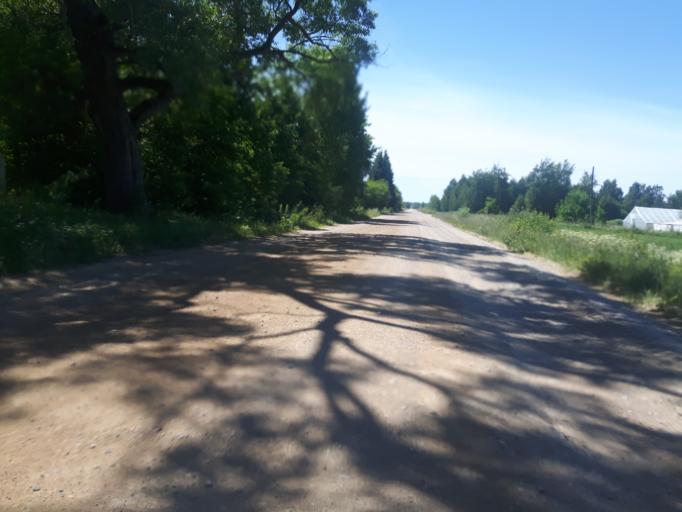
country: LV
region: Grobina
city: Grobina
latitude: 56.5276
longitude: 21.1362
